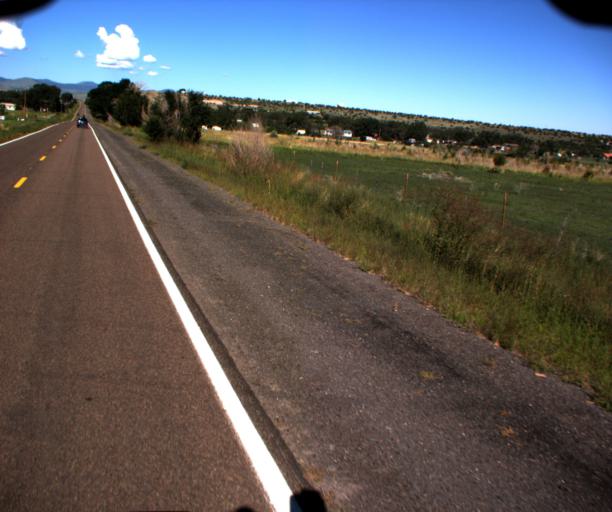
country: US
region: Arizona
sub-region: Apache County
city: Eagar
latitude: 34.1110
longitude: -109.2687
